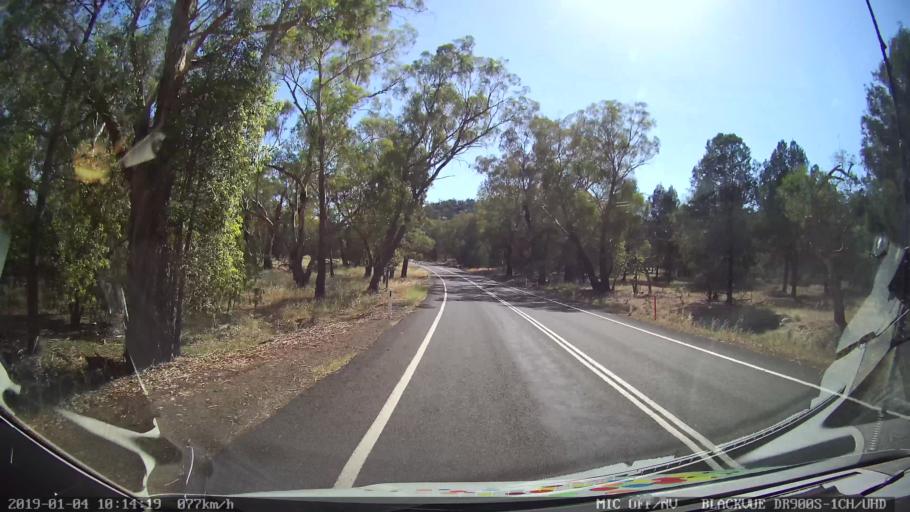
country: AU
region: New South Wales
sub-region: Cabonne
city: Canowindra
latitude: -33.3978
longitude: 148.4120
